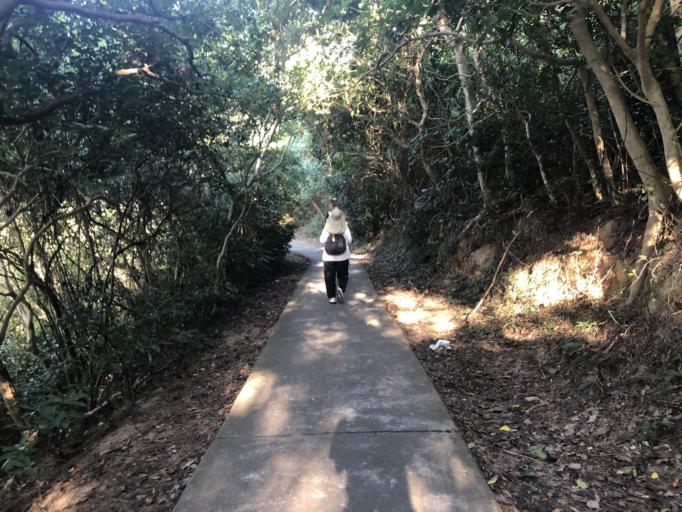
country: HK
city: Yung Shue Wan
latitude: 22.2156
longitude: 114.0282
